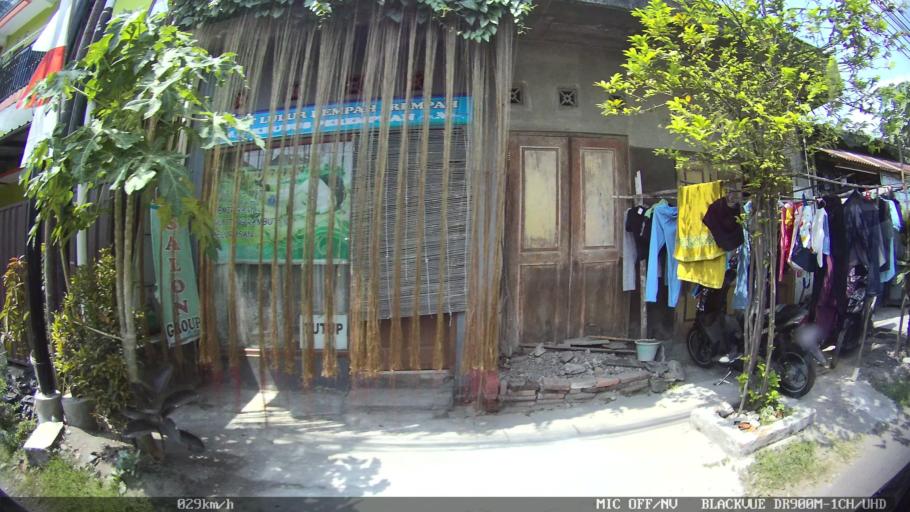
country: ID
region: Daerah Istimewa Yogyakarta
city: Yogyakarta
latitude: -7.8230
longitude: 110.4078
